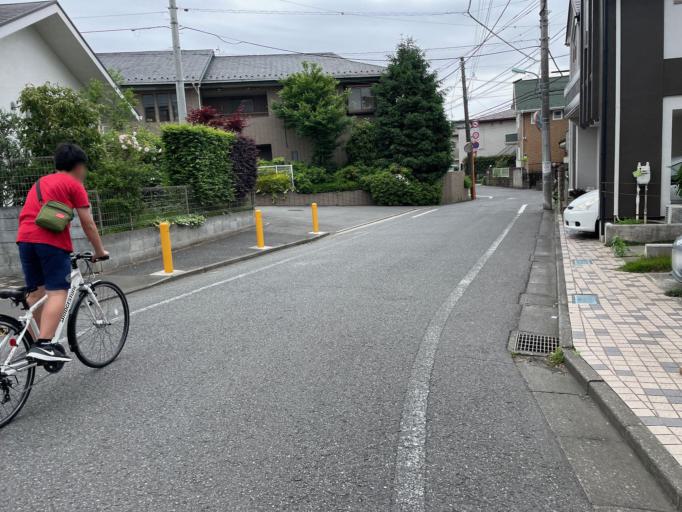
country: JP
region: Tokyo
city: Chofugaoka
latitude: 35.6560
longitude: 139.5818
